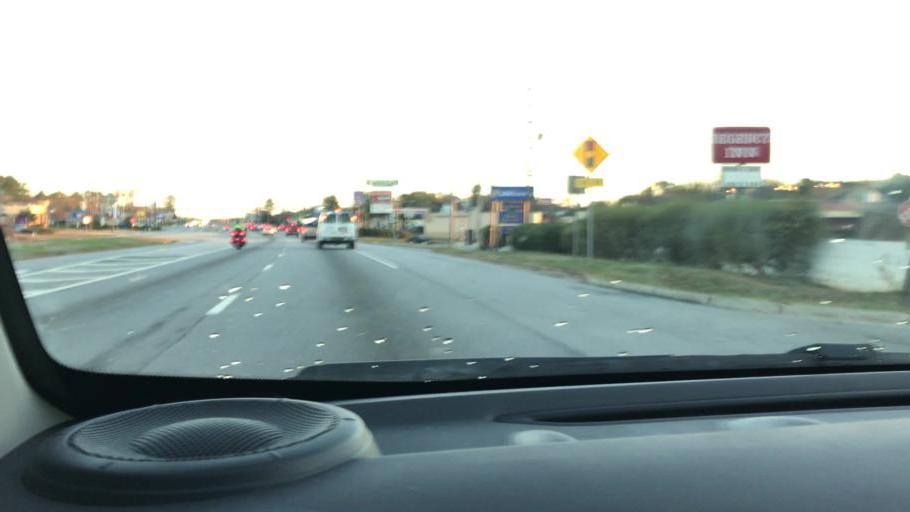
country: US
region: Georgia
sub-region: Clayton County
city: Riverdale
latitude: 33.5469
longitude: -84.4150
